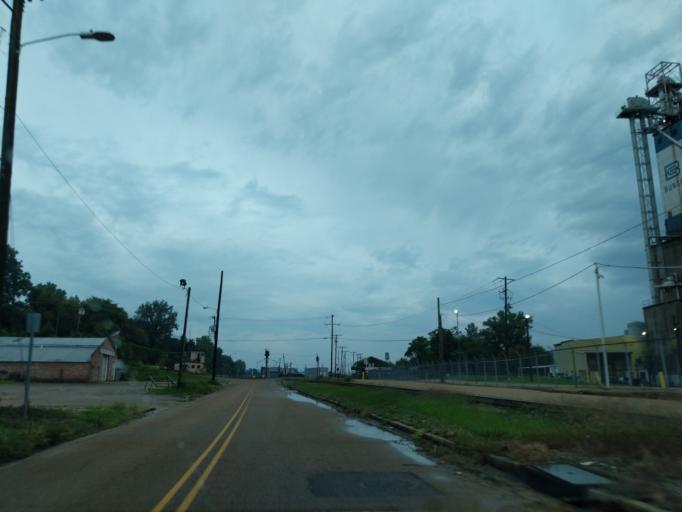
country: US
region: Mississippi
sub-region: Warren County
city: Vicksburg
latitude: 32.3470
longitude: -90.8860
